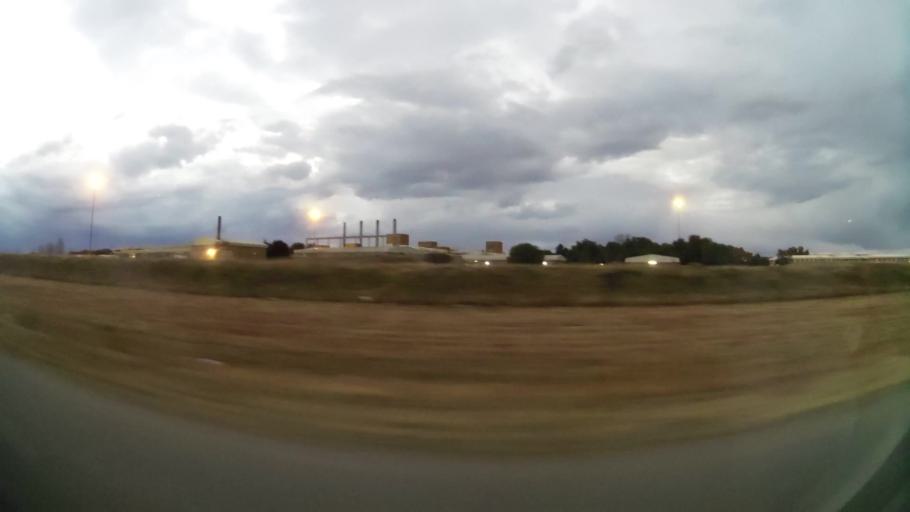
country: ZA
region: Orange Free State
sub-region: Lejweleputswa District Municipality
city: Welkom
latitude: -27.9532
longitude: 26.7889
